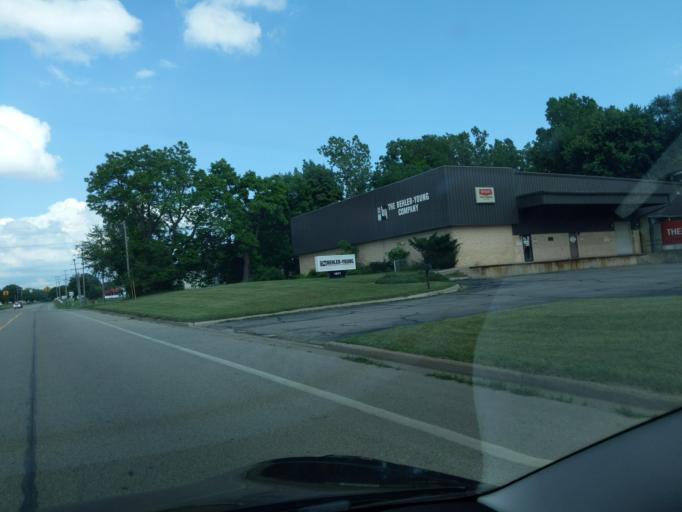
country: US
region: Michigan
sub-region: Jackson County
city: Jackson
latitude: 42.2331
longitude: -84.3864
